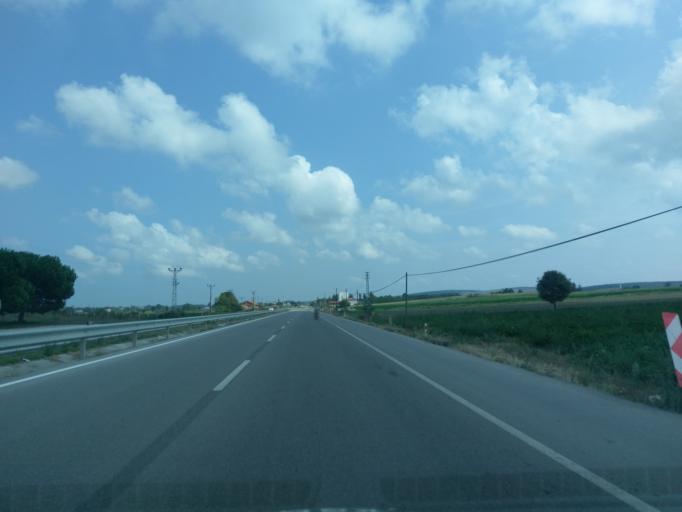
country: TR
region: Samsun
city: Bafra
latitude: 41.6016
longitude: 35.7956
